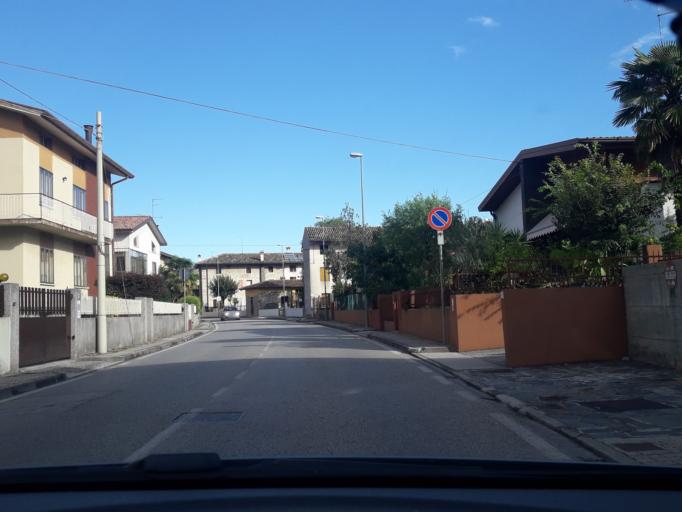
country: IT
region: Friuli Venezia Giulia
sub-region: Provincia di Udine
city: Passons
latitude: 46.0669
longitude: 13.1879
